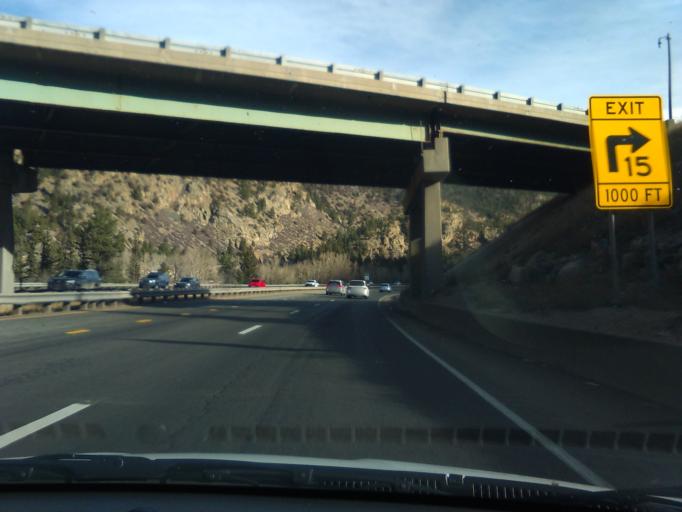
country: US
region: Colorado
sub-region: Clear Creek County
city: Georgetown
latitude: 39.7585
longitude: -105.6554
